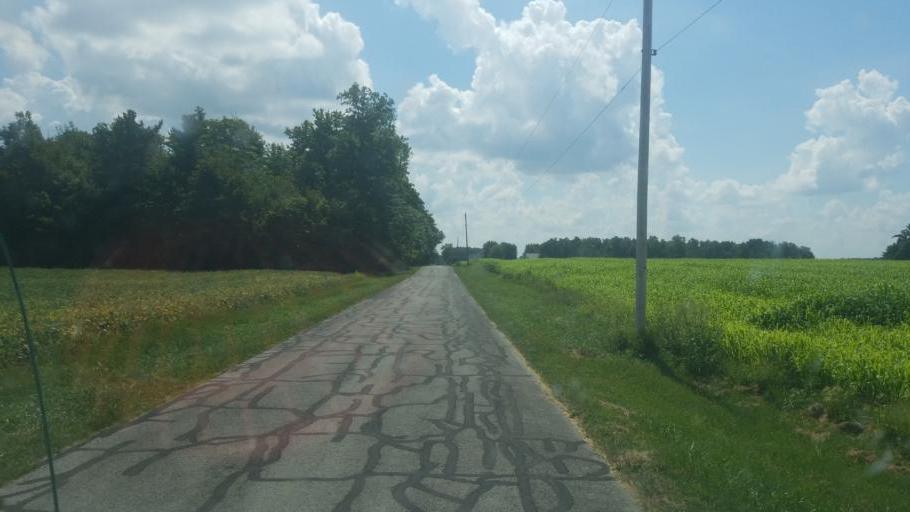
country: US
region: Ohio
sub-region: Hancock County
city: Arlington
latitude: 40.8889
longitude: -83.7080
